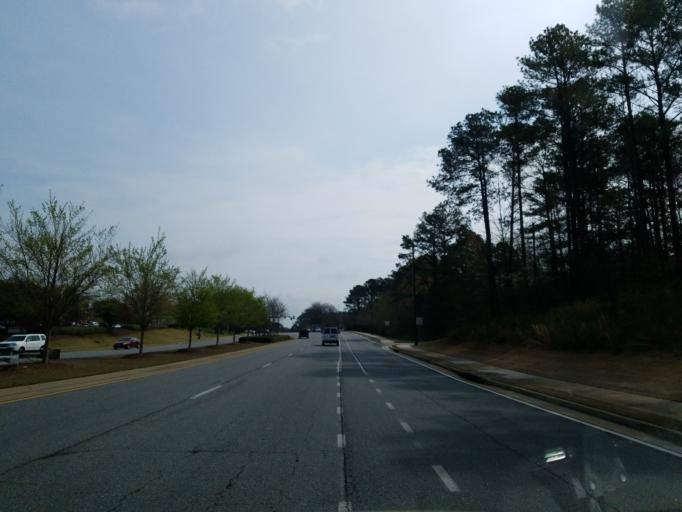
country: US
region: Georgia
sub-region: Fulton County
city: Alpharetta
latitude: 34.0874
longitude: -84.2609
